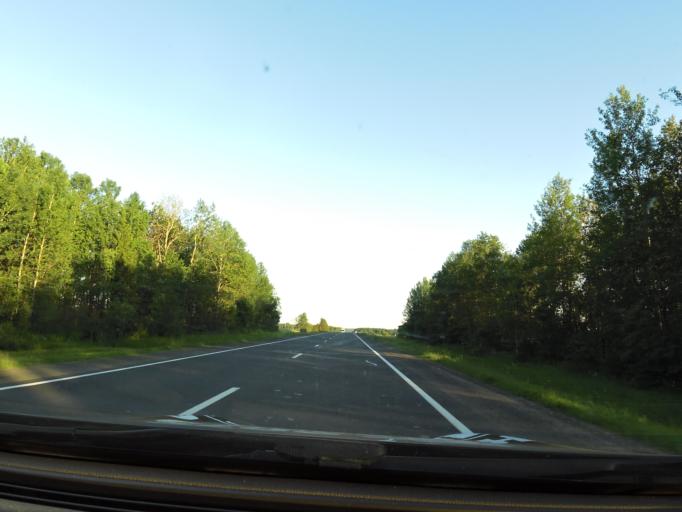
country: RU
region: Vologda
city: Gryazovets
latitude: 58.7748
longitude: 40.2748
